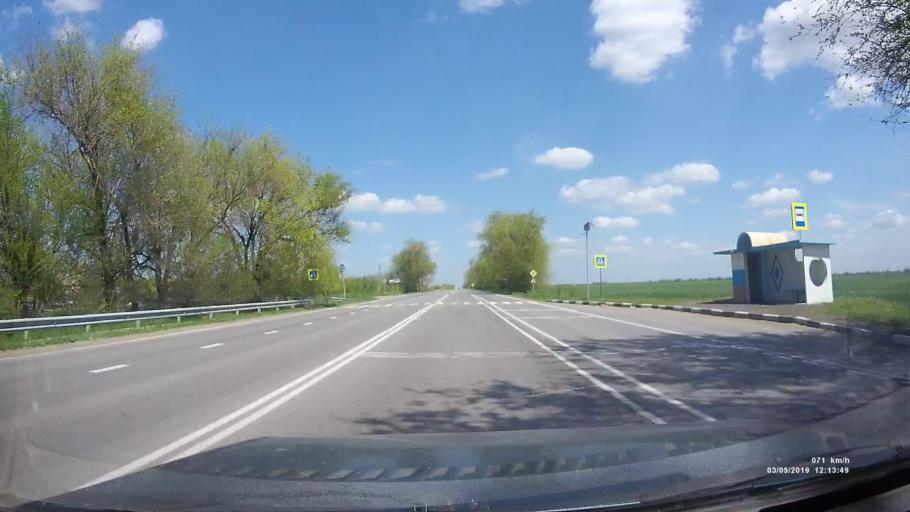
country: RU
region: Rostov
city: Melikhovskaya
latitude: 47.3364
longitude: 40.5577
